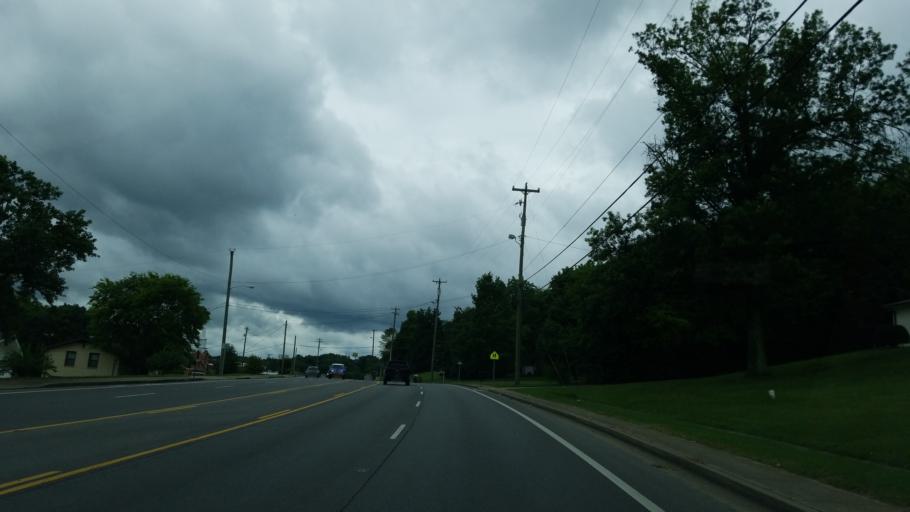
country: US
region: Tennessee
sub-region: Rutherford County
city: La Vergne
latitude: 36.0696
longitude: -86.6370
